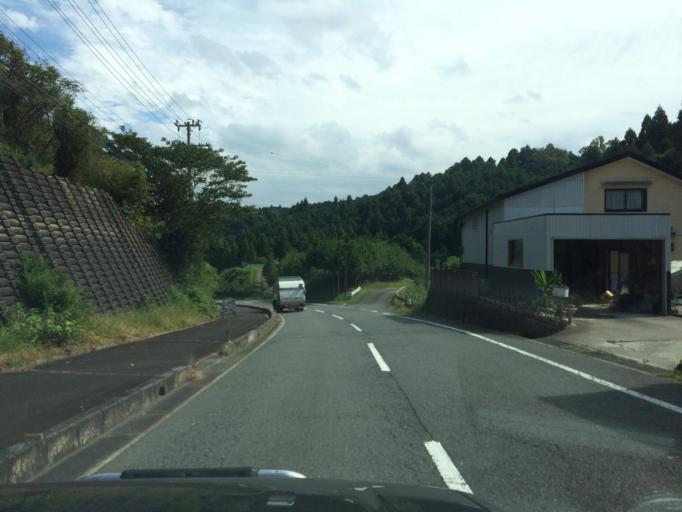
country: JP
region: Mie
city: Nabari
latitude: 34.6775
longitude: 136.0197
